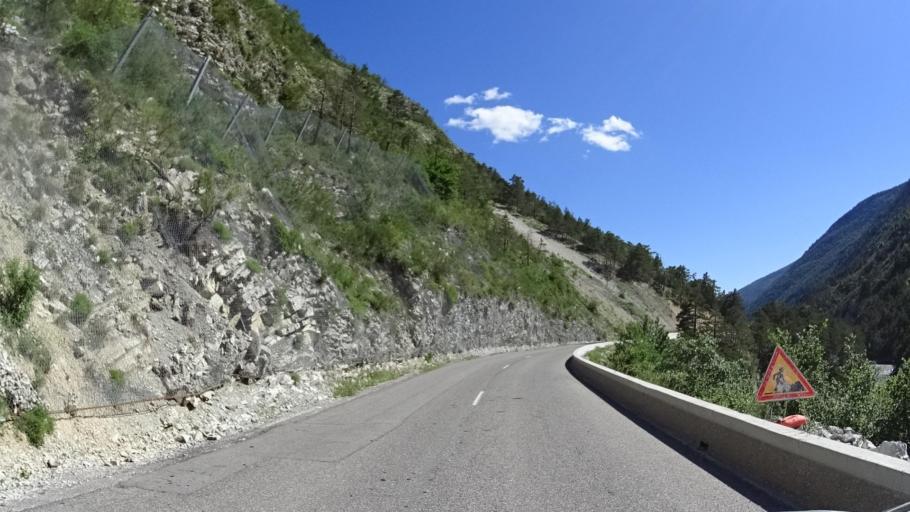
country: FR
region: Provence-Alpes-Cote d'Azur
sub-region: Departement des Alpes-de-Haute-Provence
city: Annot
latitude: 44.0605
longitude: 6.5762
